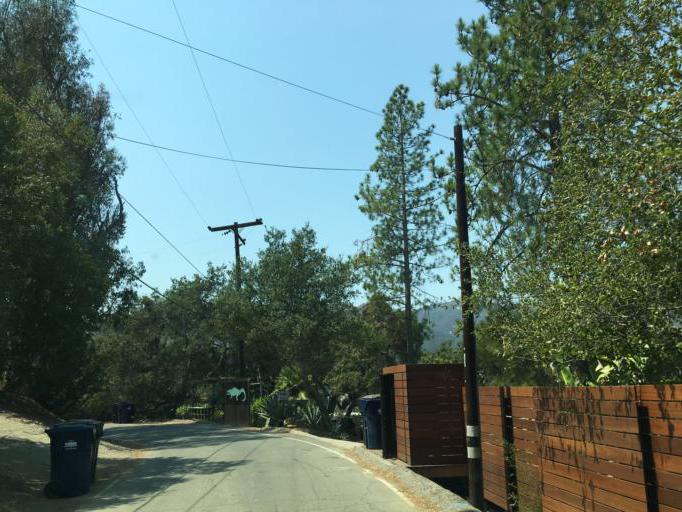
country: US
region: California
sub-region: Los Angeles County
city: Topanga
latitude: 34.0912
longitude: -118.5962
